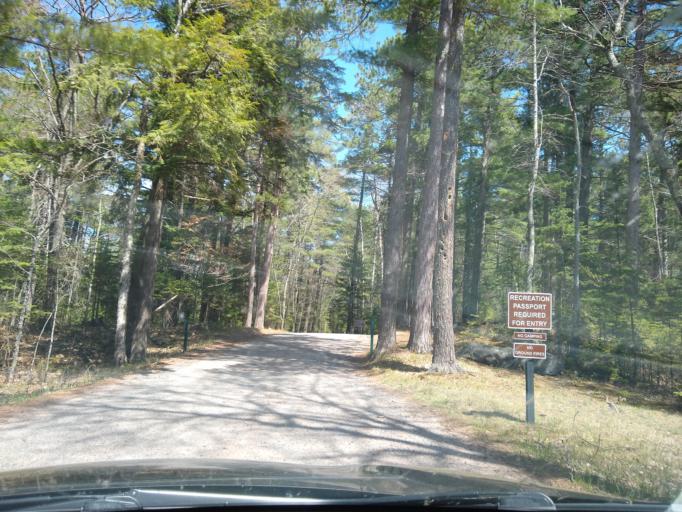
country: US
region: Michigan
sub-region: Marquette County
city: Trowbridge Park
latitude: 46.6325
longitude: -87.4745
